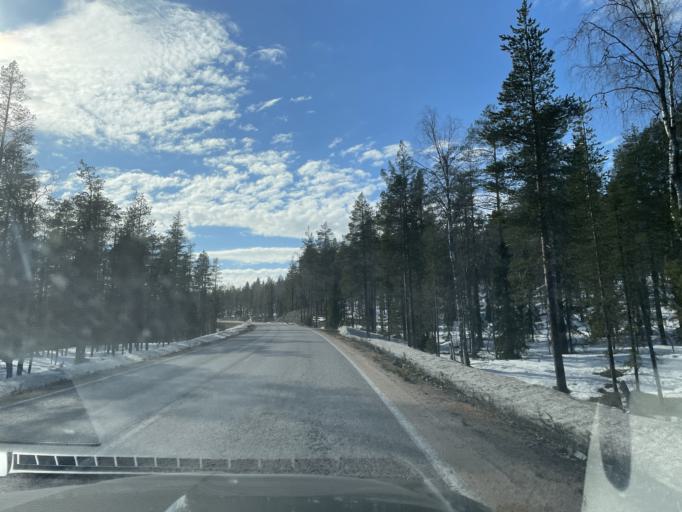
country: FI
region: Lapland
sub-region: Tunturi-Lappi
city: Kolari
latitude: 67.5396
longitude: 24.2374
